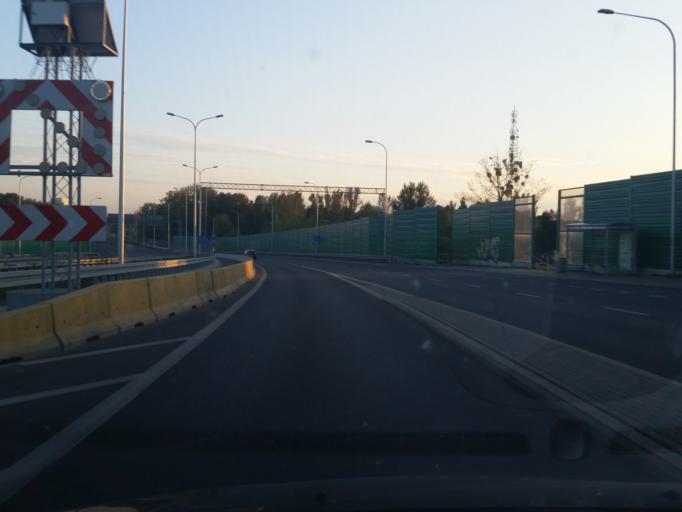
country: PL
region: Masovian Voivodeship
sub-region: Warszawa
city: Bielany
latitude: 52.2988
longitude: 20.9353
